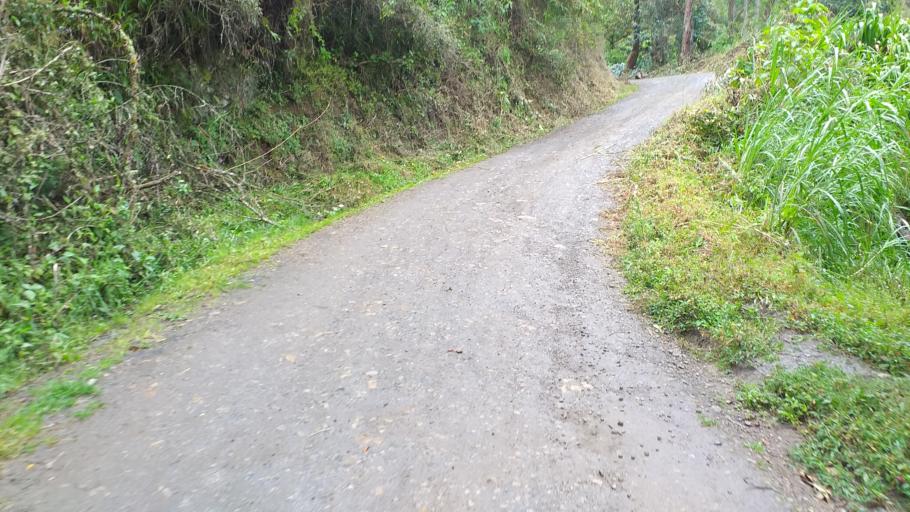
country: CO
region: Cundinamarca
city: Tenza
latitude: 5.1139
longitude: -73.4521
